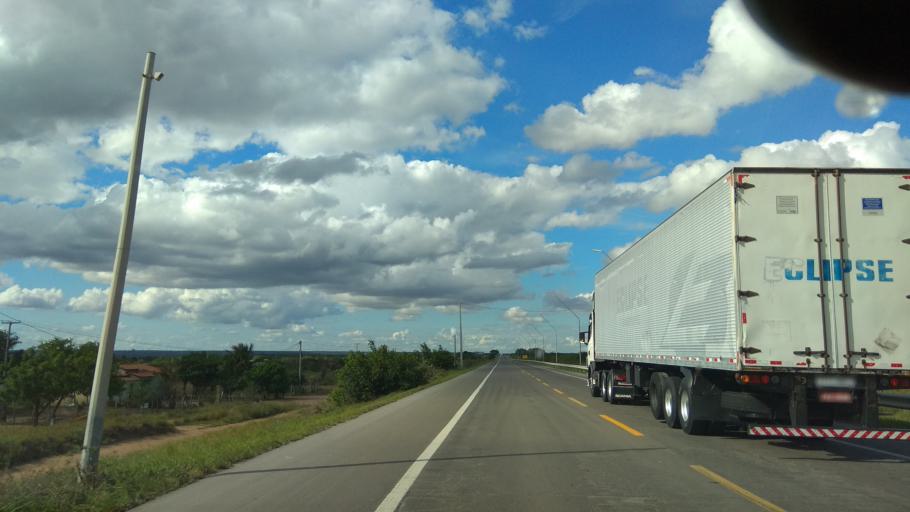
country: BR
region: Bahia
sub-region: Castro Alves
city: Castro Alves
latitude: -12.6127
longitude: -39.5683
